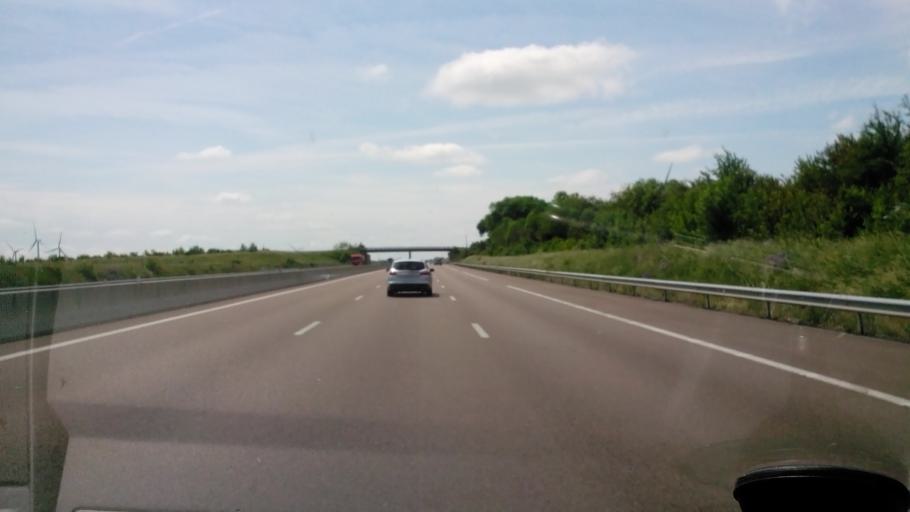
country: FR
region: Bourgogne
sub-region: Departement de la Cote-d'Or
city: Selongey
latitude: 47.7110
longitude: 5.1904
